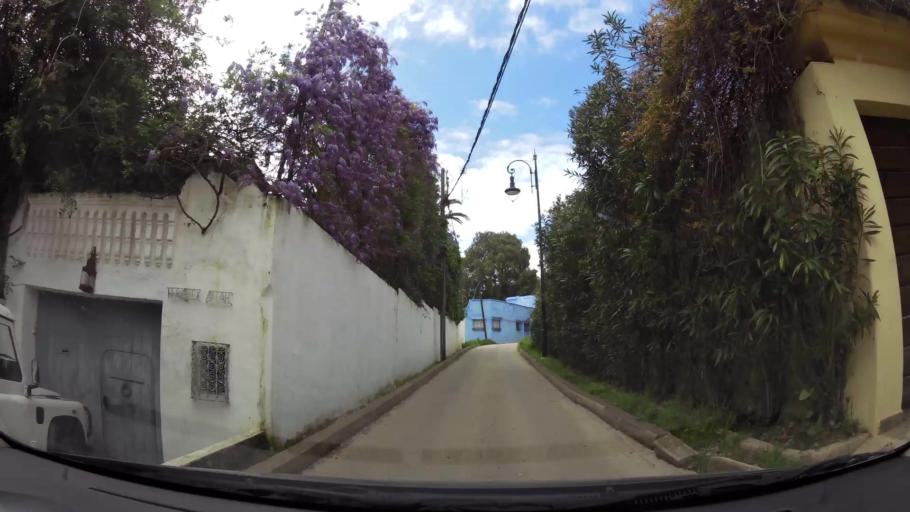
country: MA
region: Tanger-Tetouan
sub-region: Tanger-Assilah
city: Tangier
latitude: 35.7853
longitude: -5.8507
